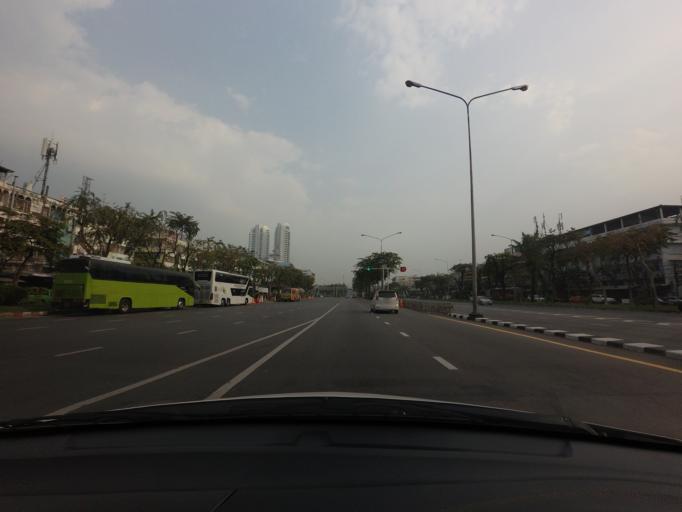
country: TH
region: Bangkok
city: Bangkok Noi
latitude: 13.7666
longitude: 100.4874
